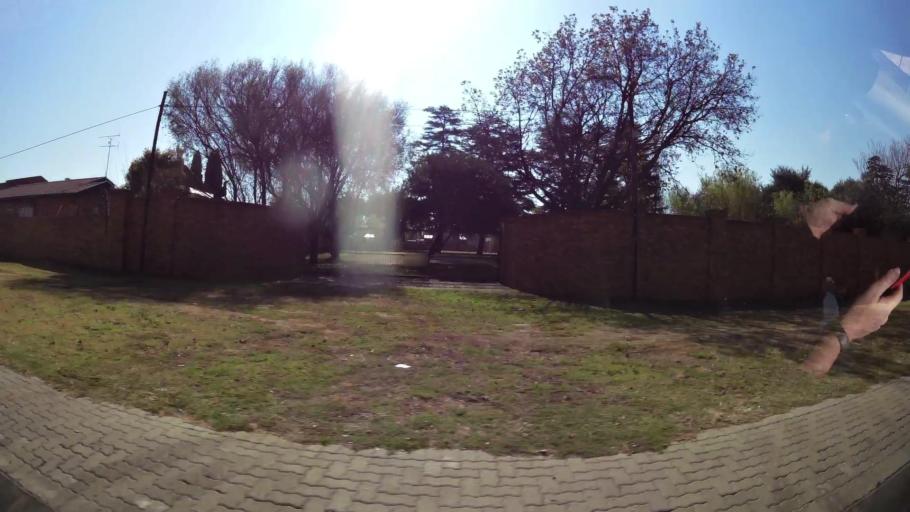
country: ZA
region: Gauteng
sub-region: Ekurhuleni Metropolitan Municipality
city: Boksburg
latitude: -26.1678
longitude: 28.2576
